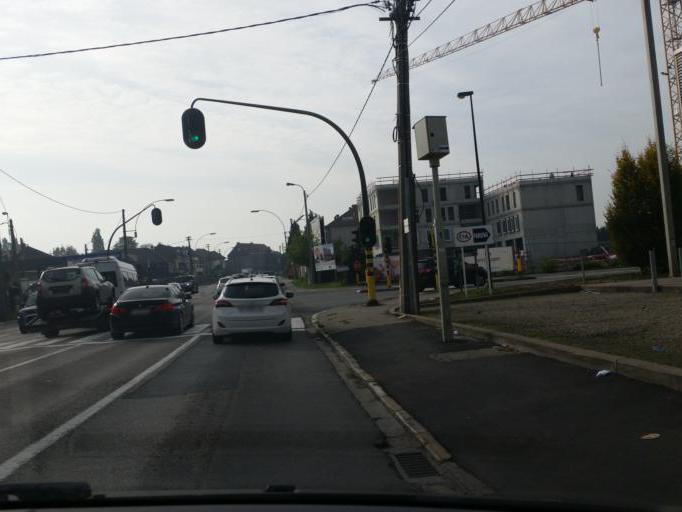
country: BE
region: Flanders
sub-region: Provincie Vlaams-Brabant
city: Drogenbos
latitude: 50.8023
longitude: 4.2885
